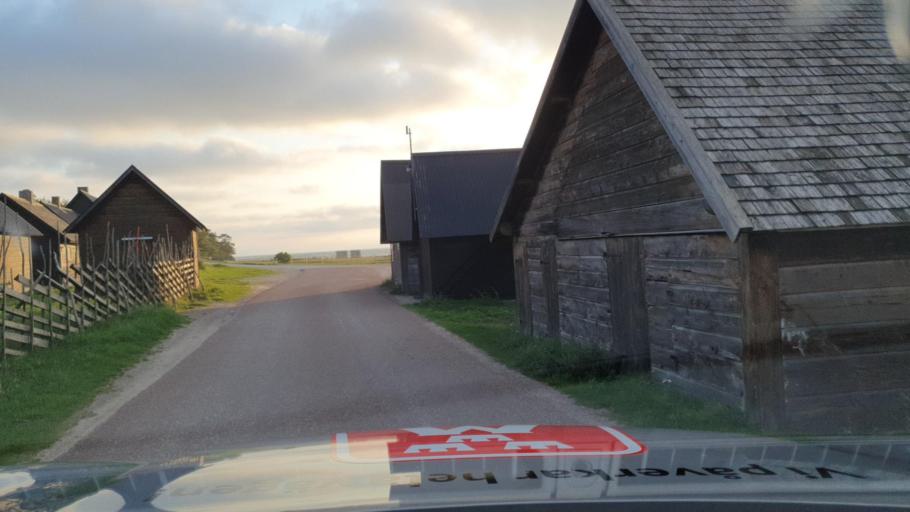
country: SE
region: Gotland
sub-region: Gotland
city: Klintehamn
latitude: 57.3078
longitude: 18.1496
